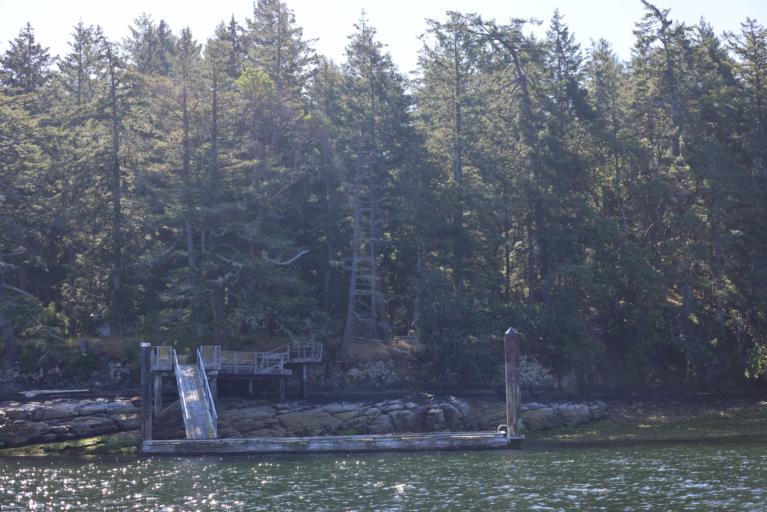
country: CA
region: British Columbia
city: North Cowichan
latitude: 48.8040
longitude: -123.5961
